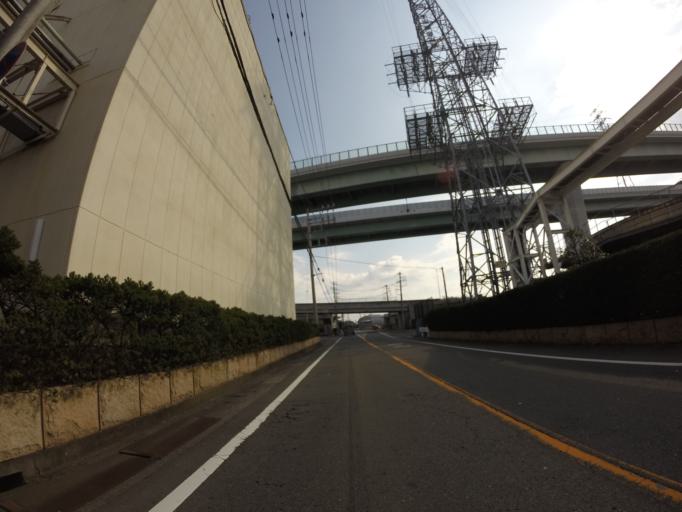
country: JP
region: Shizuoka
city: Fujinomiya
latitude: 35.1975
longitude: 138.6403
